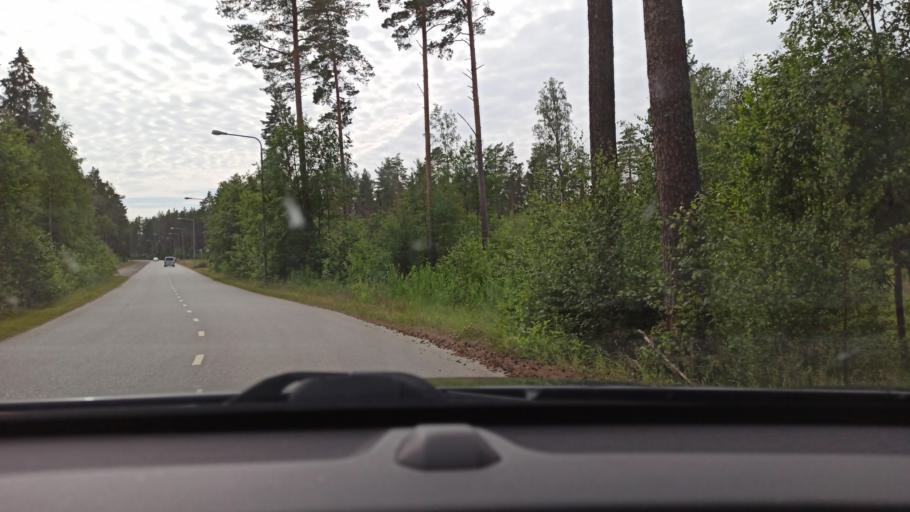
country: FI
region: Satakunta
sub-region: Pori
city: Luvia
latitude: 61.5748
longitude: 21.5236
